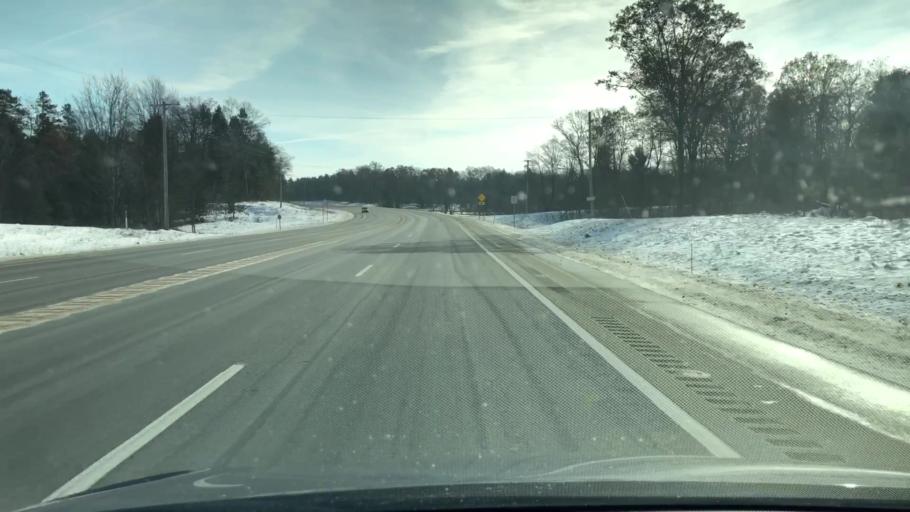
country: US
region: Michigan
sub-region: Kalkaska County
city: Kalkaska
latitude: 44.7462
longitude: -85.2226
